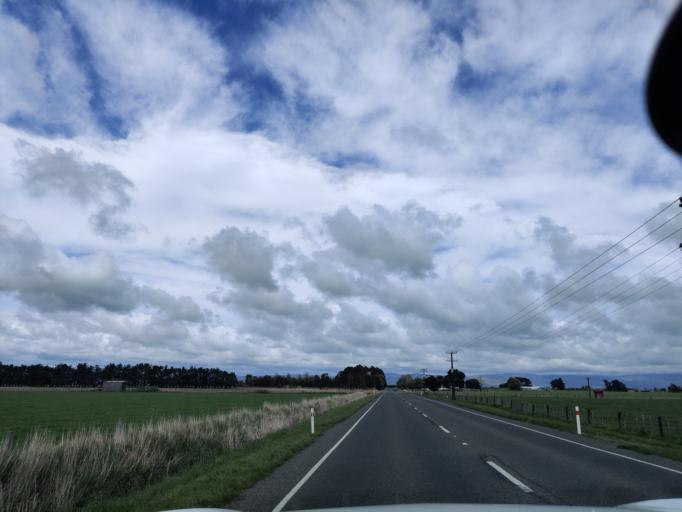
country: NZ
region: Manawatu-Wanganui
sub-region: Palmerston North City
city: Palmerston North
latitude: -40.3224
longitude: 175.5016
